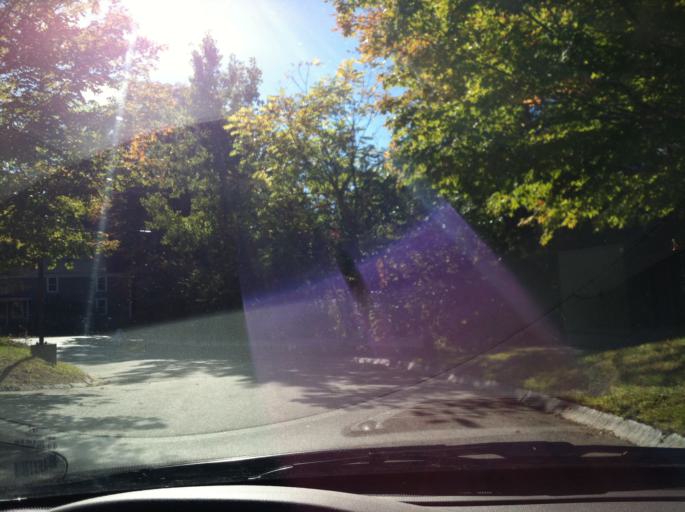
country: US
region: Massachusetts
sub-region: Middlesex County
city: Carlisle
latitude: 42.5296
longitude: -71.3507
